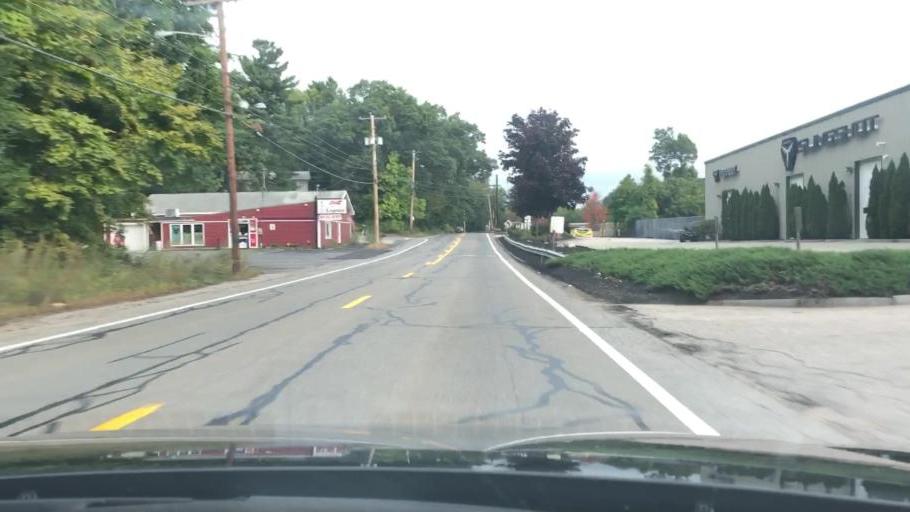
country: US
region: Massachusetts
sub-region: Middlesex County
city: Tyngsboro
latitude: 42.6543
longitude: -71.4016
